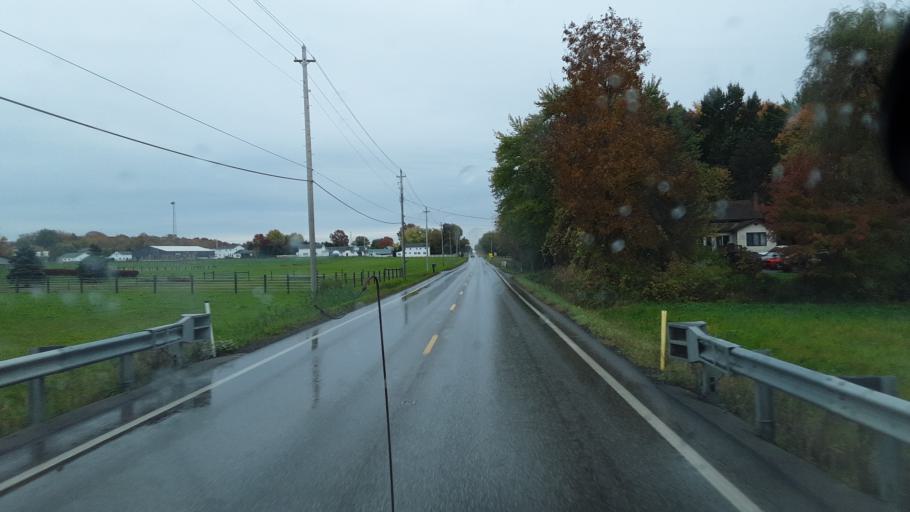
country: US
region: Ohio
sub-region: Geauga County
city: Middlefield
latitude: 41.4298
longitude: -81.1081
